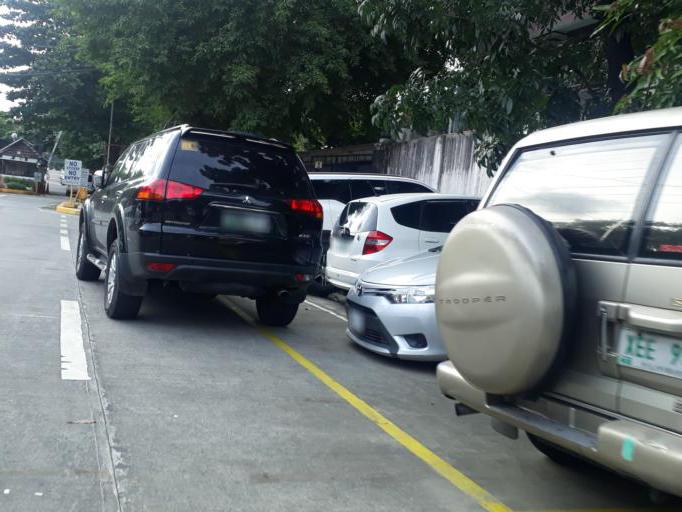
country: PH
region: Metro Manila
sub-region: Marikina
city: Calumpang
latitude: 14.6368
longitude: 121.0718
